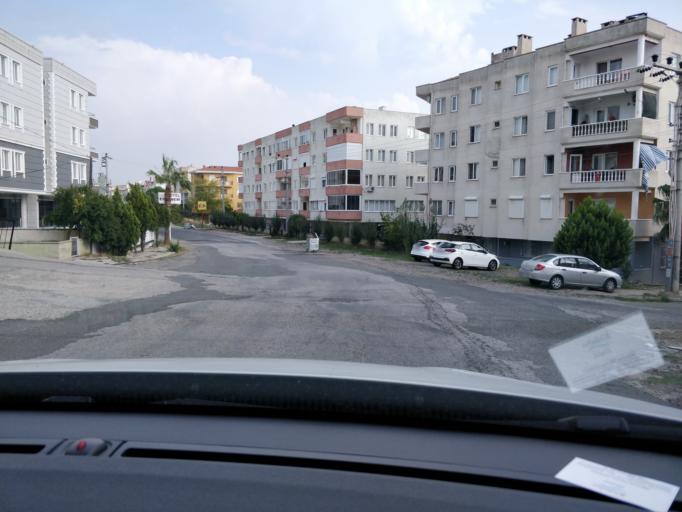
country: TR
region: Balikesir
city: Ayvalik
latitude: 39.2733
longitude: 26.6513
